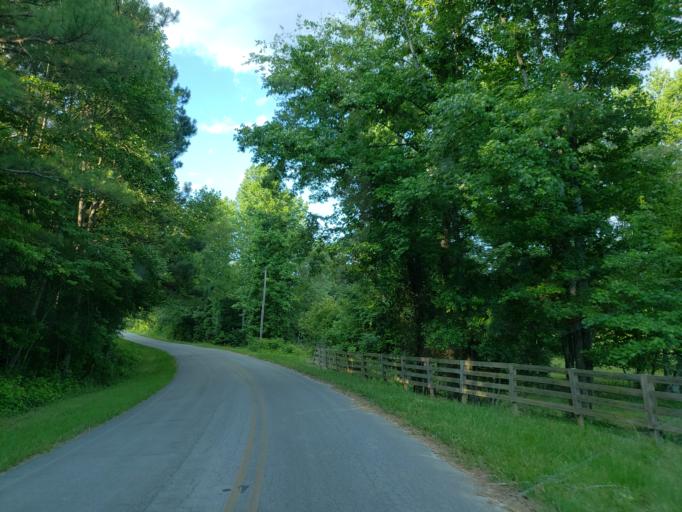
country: US
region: Georgia
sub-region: Haralson County
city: Tallapoosa
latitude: 33.8249
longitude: -85.2801
